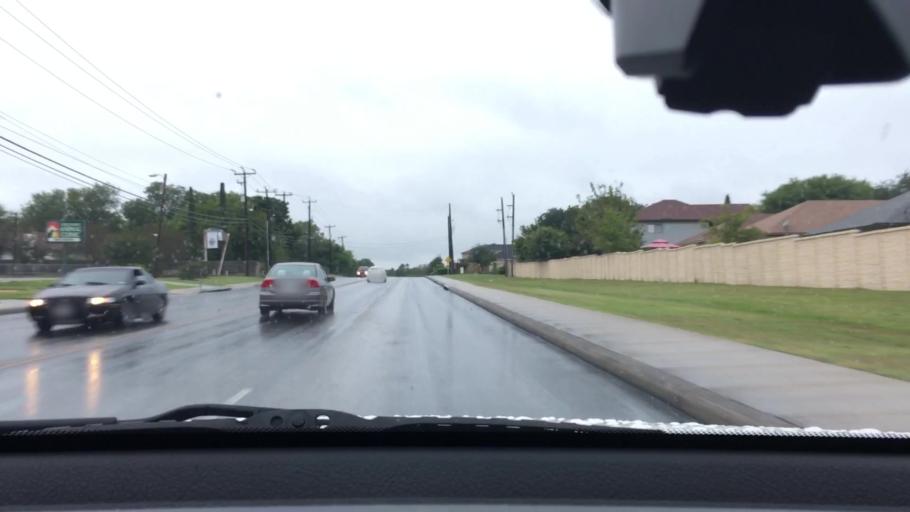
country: US
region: Texas
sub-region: Bexar County
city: Windcrest
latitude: 29.5216
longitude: -98.3574
